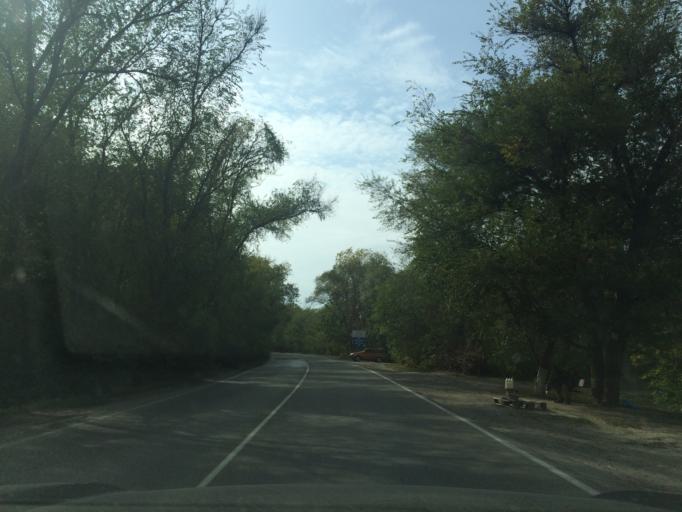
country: RU
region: Rostov
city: Kalinin
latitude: 47.1761
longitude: 39.5639
